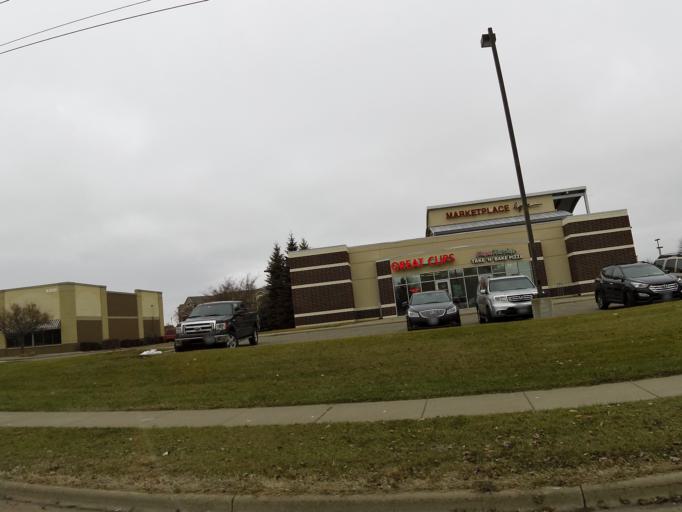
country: US
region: Minnesota
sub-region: Scott County
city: Prior Lake
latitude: 44.7465
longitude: -93.3832
